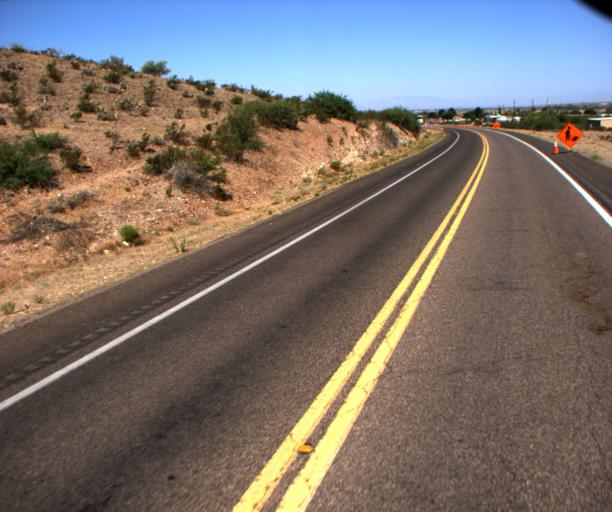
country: US
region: Arizona
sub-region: Graham County
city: Safford
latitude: 32.8124
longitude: -109.5920
